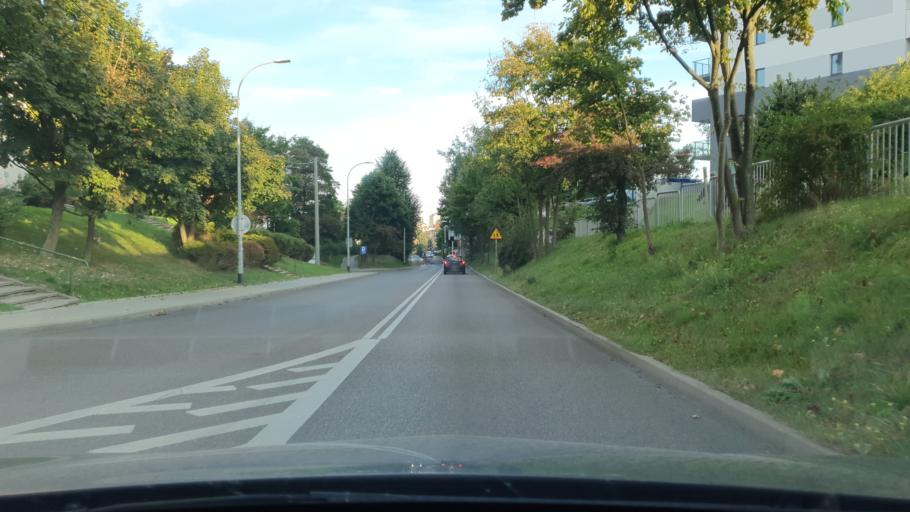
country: PL
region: Pomeranian Voivodeship
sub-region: Powiat gdanski
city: Kowale
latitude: 54.3582
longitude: 18.5887
